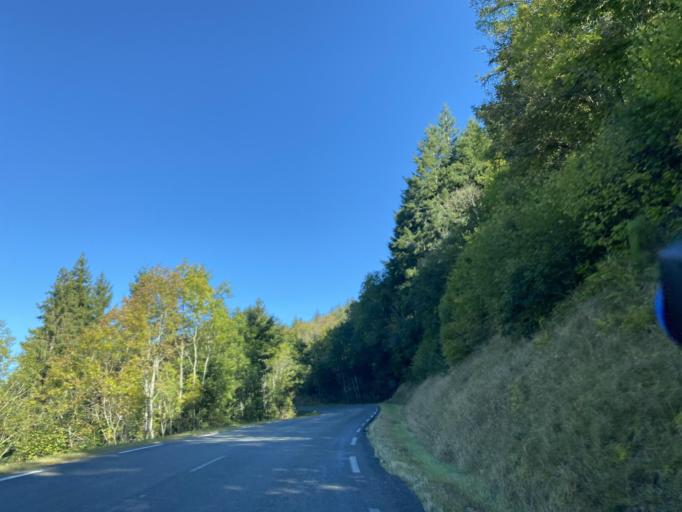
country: FR
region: Rhone-Alpes
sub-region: Departement de la Loire
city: Saint-Just-en-Chevalet
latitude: 45.9280
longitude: 3.8521
